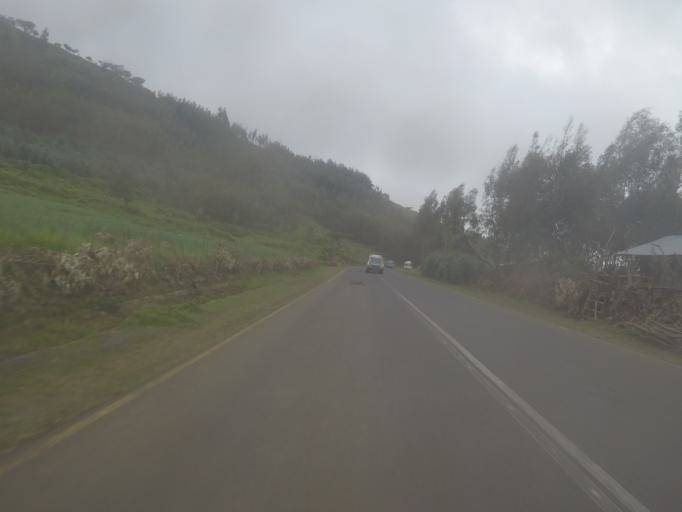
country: ET
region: Amhara
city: Gondar
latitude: 12.7283
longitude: 37.5122
